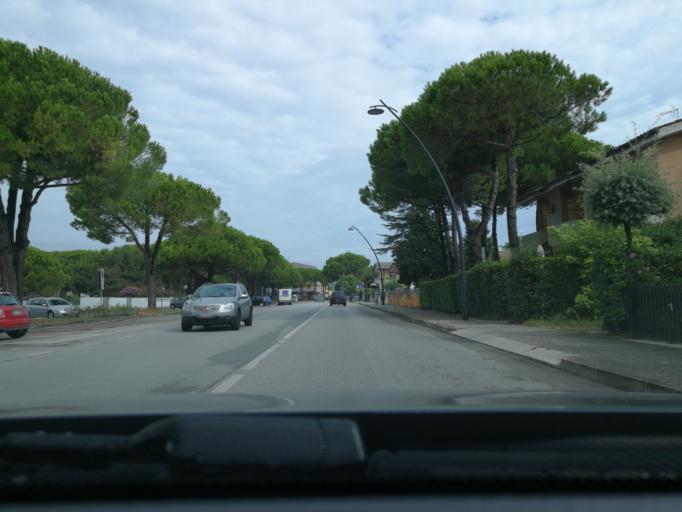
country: IT
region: Veneto
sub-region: Provincia di Venezia
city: Bibione
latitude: 45.6411
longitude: 13.0547
